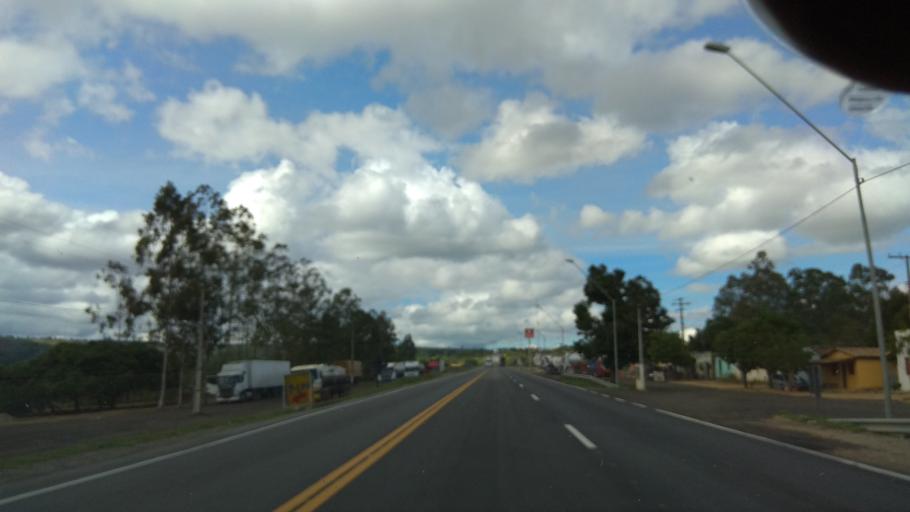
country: BR
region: Bahia
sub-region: Santa Ines
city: Santa Ines
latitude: -13.1045
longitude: -39.9912
